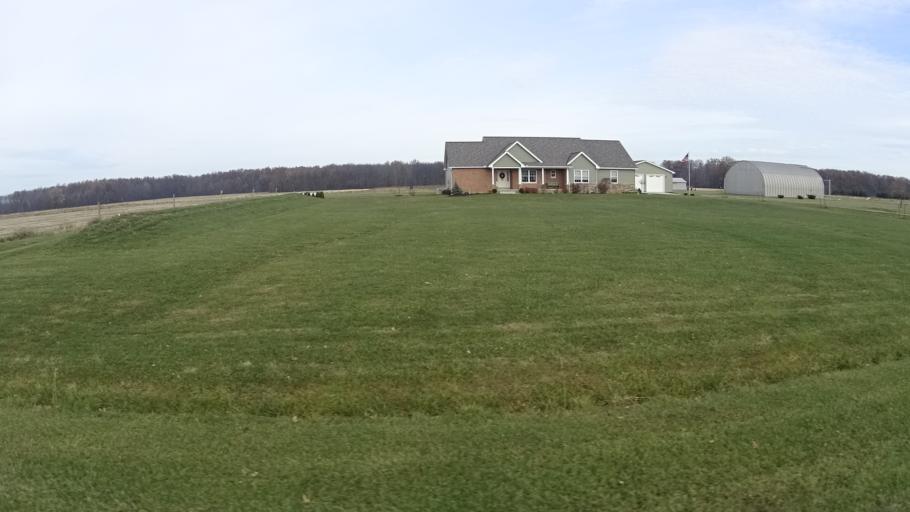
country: US
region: Ohio
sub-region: Lorain County
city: Eaton Estates
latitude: 41.2600
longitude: -81.9908
